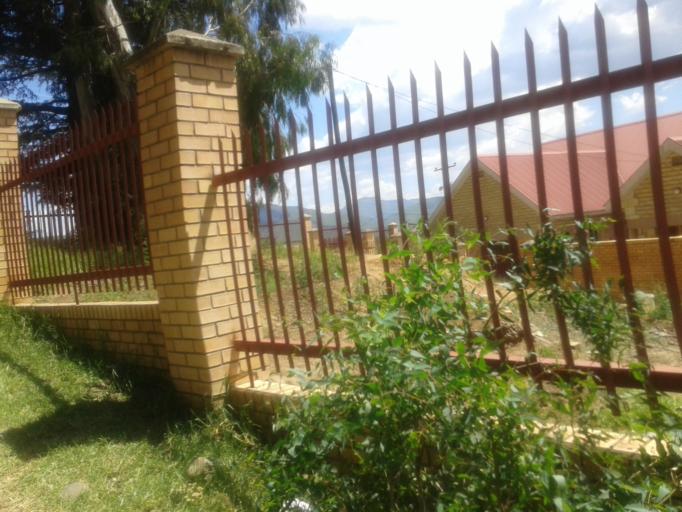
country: LS
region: Qacha's Nek
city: Qacha's Nek
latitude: -30.1193
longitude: 28.6870
